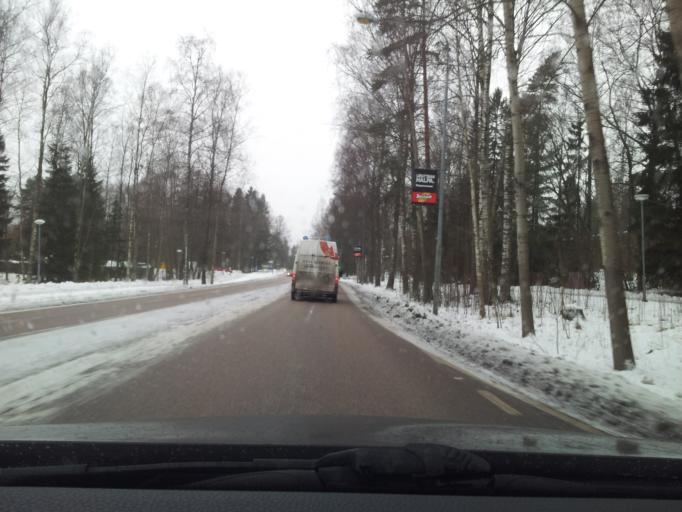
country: FI
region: Uusimaa
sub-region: Helsinki
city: Koukkuniemi
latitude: 60.1735
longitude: 24.7908
